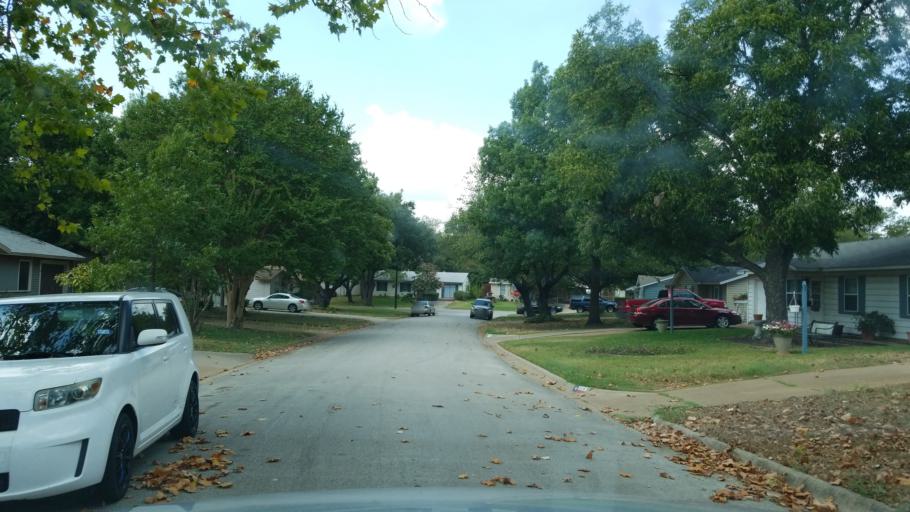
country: US
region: Texas
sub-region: Tarrant County
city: Euless
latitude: 32.8494
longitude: -97.0843
